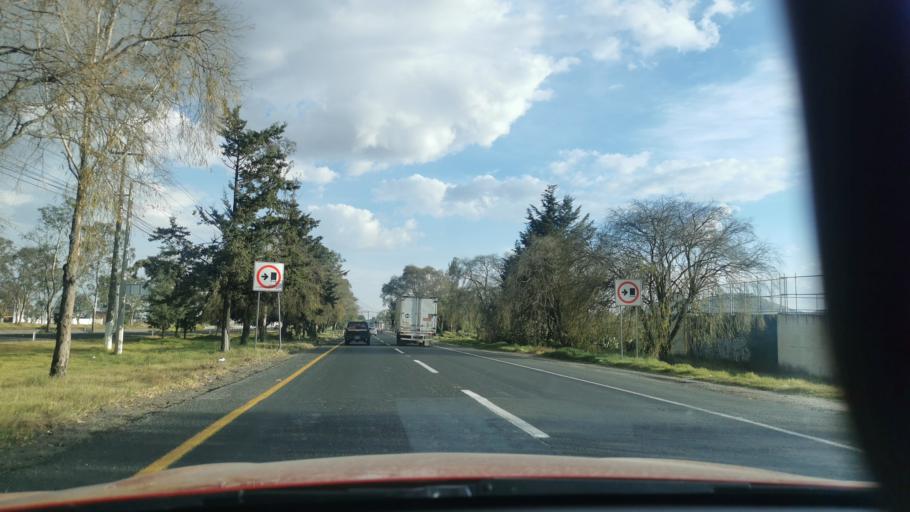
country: MX
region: Mexico
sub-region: Toluca
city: Colonia Aviacion Autopan
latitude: 19.3718
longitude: -99.6970
